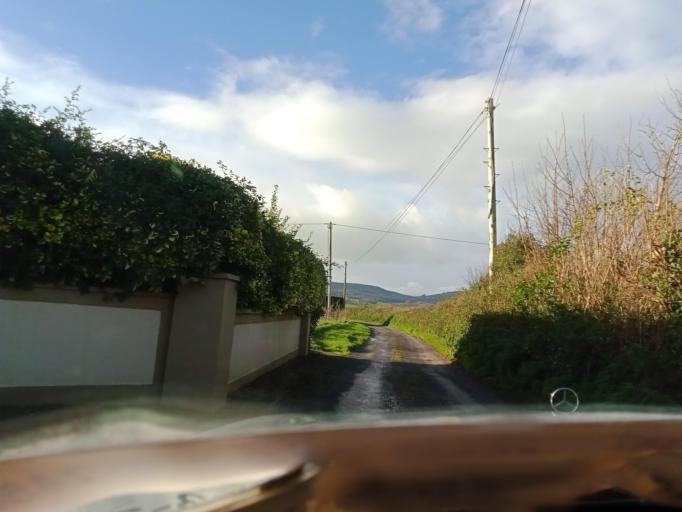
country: IE
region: Leinster
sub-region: Kilkenny
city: Mooncoin
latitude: 52.2801
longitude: -7.2525
